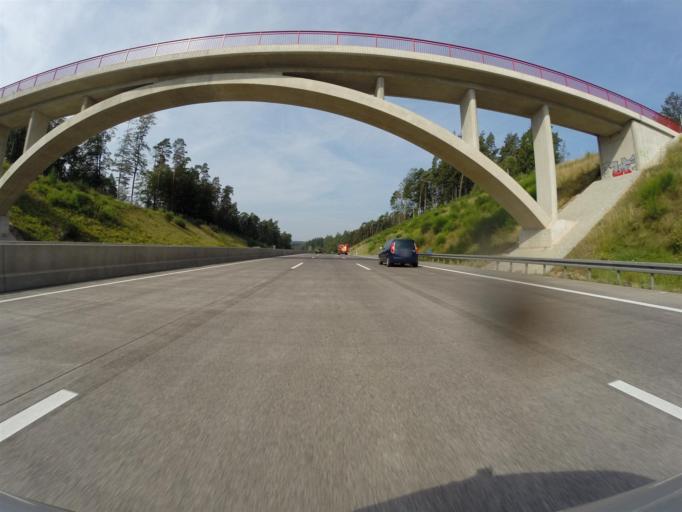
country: DE
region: Hesse
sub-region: Regierungsbezirk Kassel
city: Niederaula
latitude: 50.8411
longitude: 9.6167
